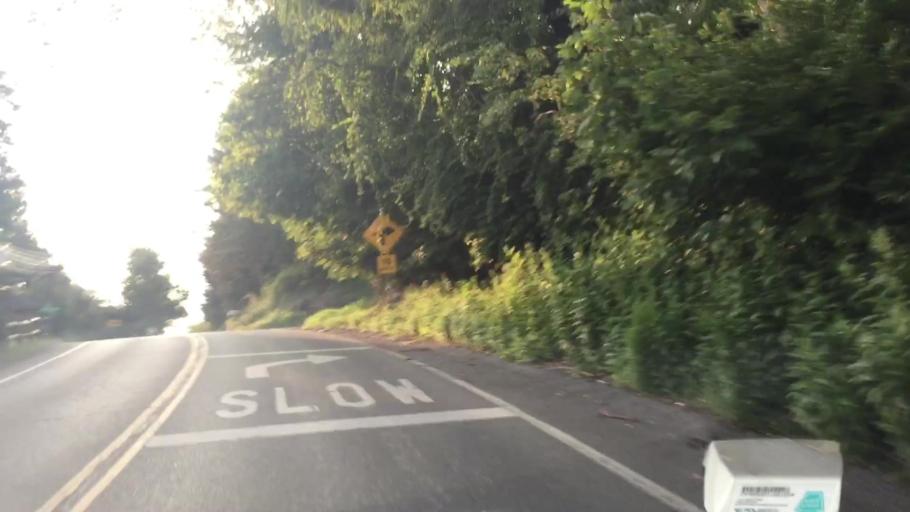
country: US
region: Pennsylvania
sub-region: Allegheny County
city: Franklin Park
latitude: 40.5753
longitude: -80.0534
